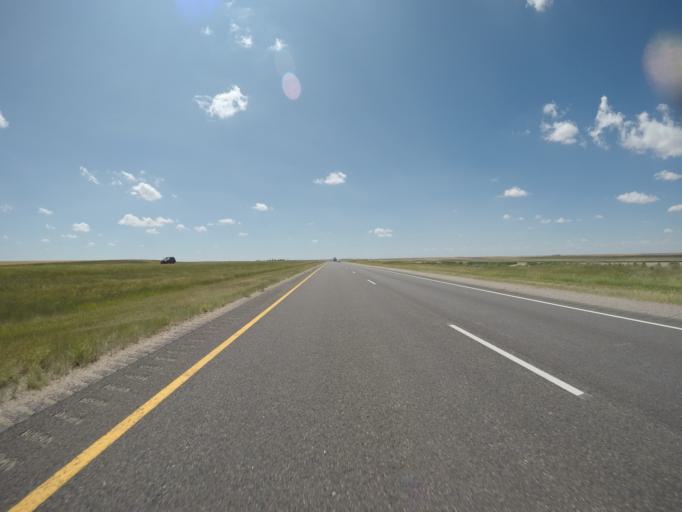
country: US
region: Colorado
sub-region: Lincoln County
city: Hugo
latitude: 39.2861
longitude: -103.1879
